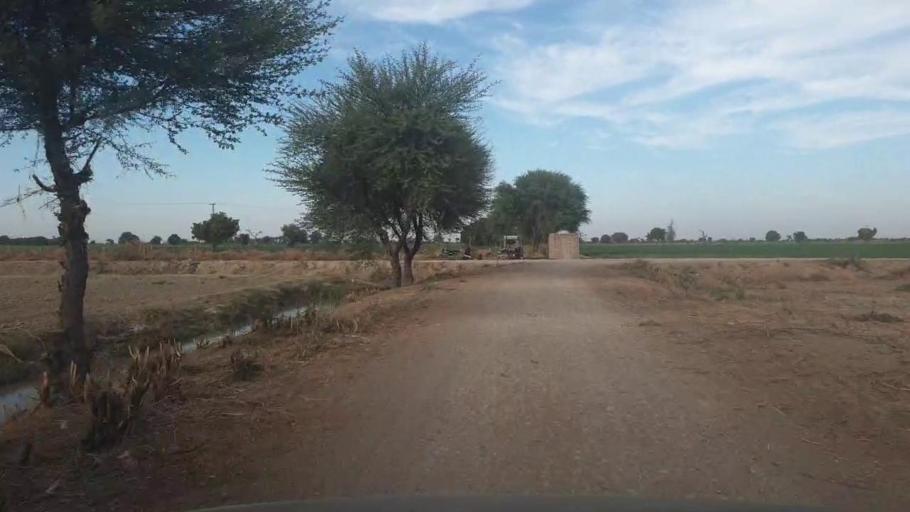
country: PK
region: Sindh
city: Samaro
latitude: 25.3312
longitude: 69.2560
